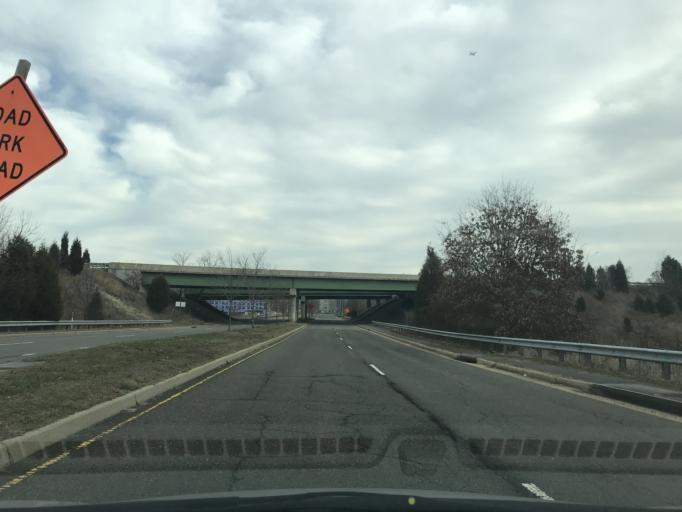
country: US
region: Virginia
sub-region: City of Manassas
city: Manassas
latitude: 38.7382
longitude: -77.5165
